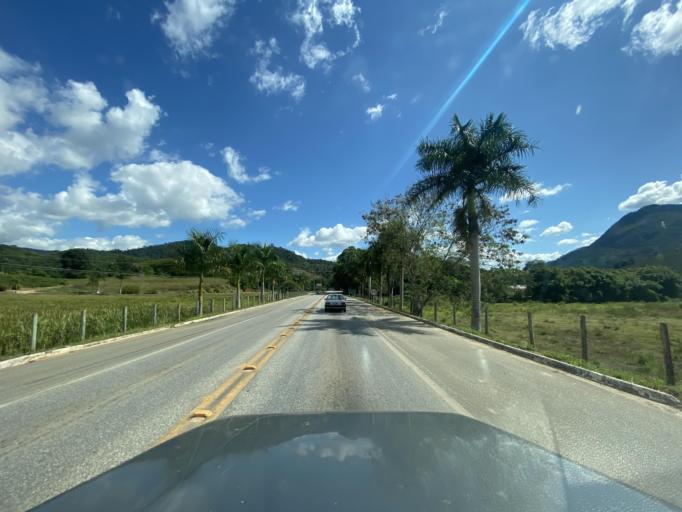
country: BR
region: Espirito Santo
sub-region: Jeronimo Monteiro
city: Jeronimo Monteiro
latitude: -20.7617
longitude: -41.4551
